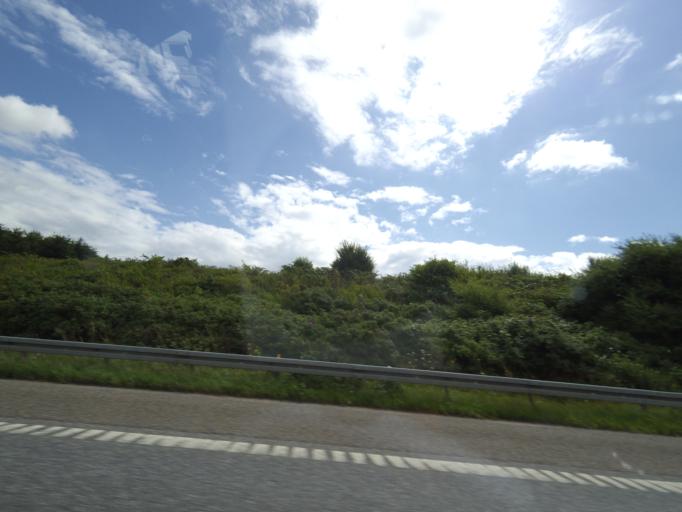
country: DK
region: Central Jutland
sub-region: Skanderborg Kommune
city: Horning
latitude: 56.0898
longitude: 10.0178
